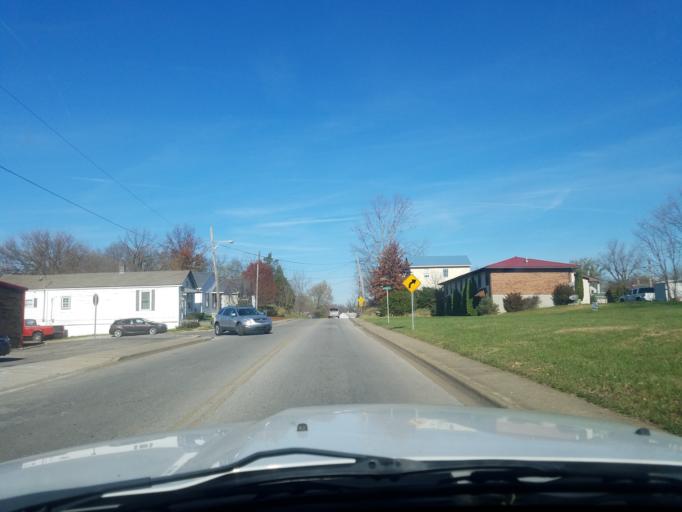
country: US
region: Indiana
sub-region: Floyd County
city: New Albany
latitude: 38.2919
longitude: -85.8260
